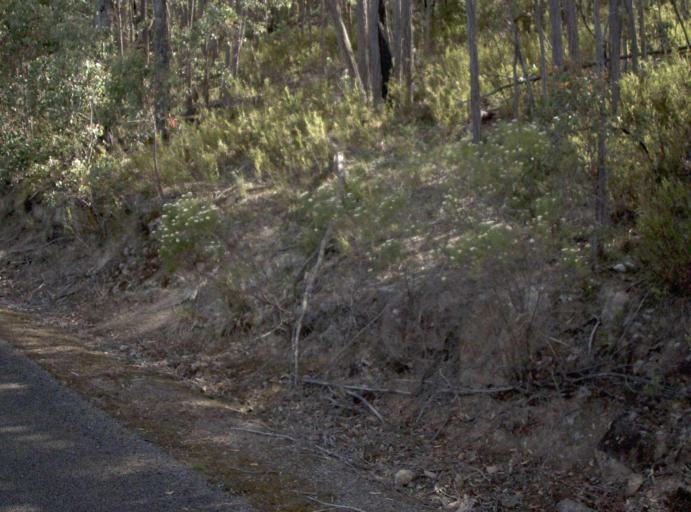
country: AU
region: Victoria
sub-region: East Gippsland
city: Lakes Entrance
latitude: -37.4807
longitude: 148.1245
